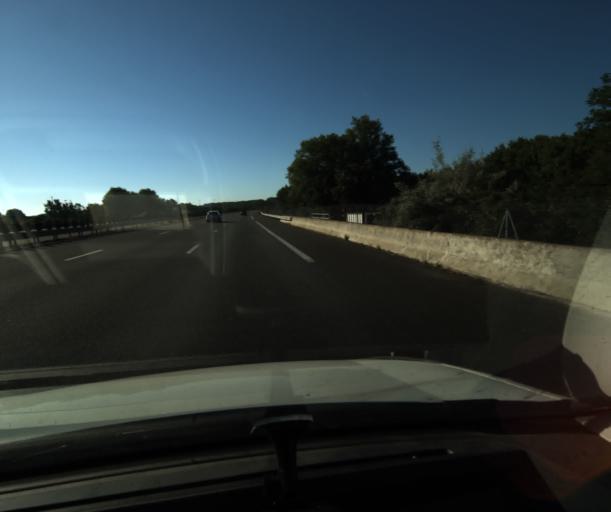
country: FR
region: Midi-Pyrenees
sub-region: Departement de la Haute-Garonne
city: Castelnau-d'Estretefonds
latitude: 43.8121
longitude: 1.3603
